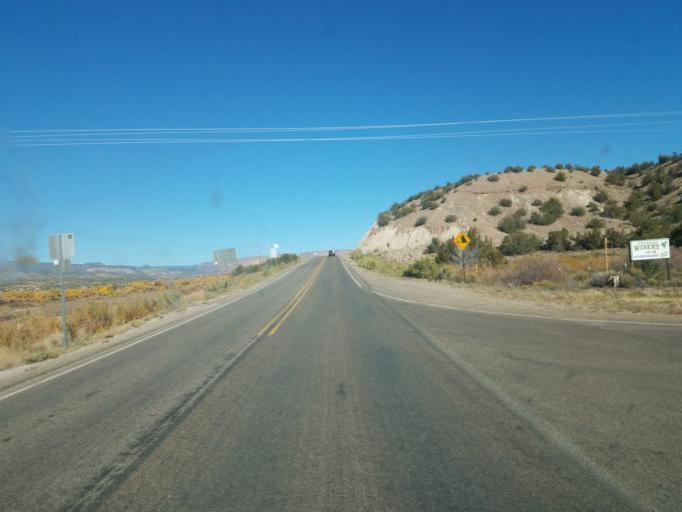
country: US
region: New Mexico
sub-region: Sandoval County
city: Jemez Pueblo
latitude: 35.6257
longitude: -106.7243
